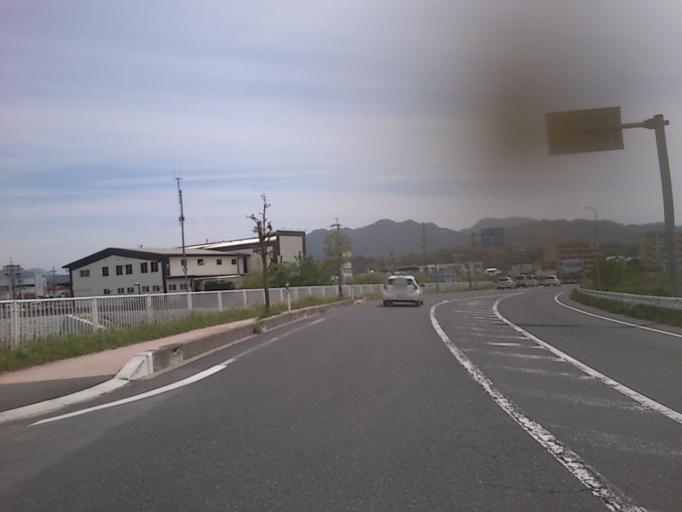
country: JP
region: Kyoto
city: Miyazu
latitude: 35.6105
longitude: 135.0803
